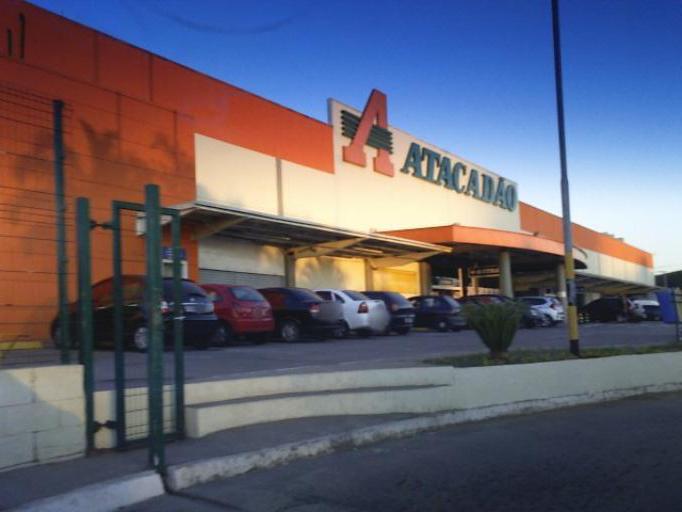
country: BR
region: Sao Paulo
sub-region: Sao Jose Dos Campos
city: Sao Jose dos Campos
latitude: -23.1796
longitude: -45.8667
